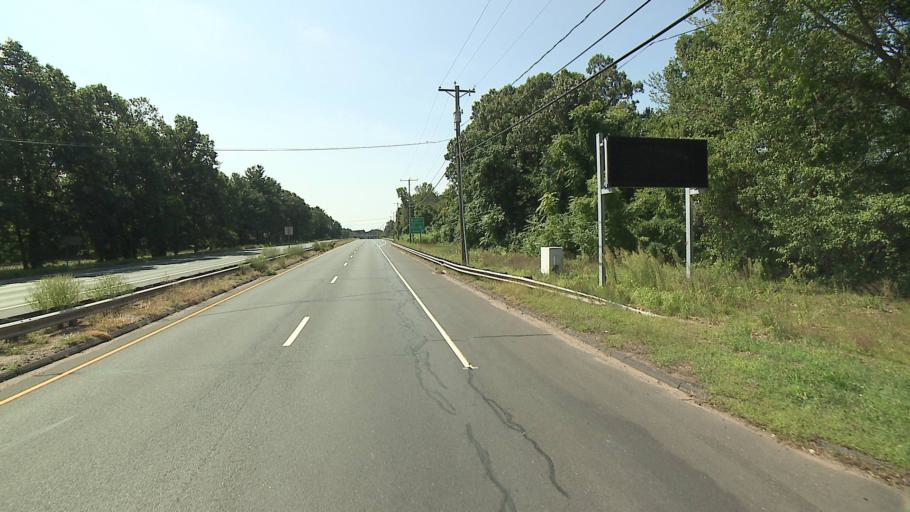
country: US
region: Connecticut
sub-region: Hartford County
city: South Windsor
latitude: 41.8113
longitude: -72.6125
